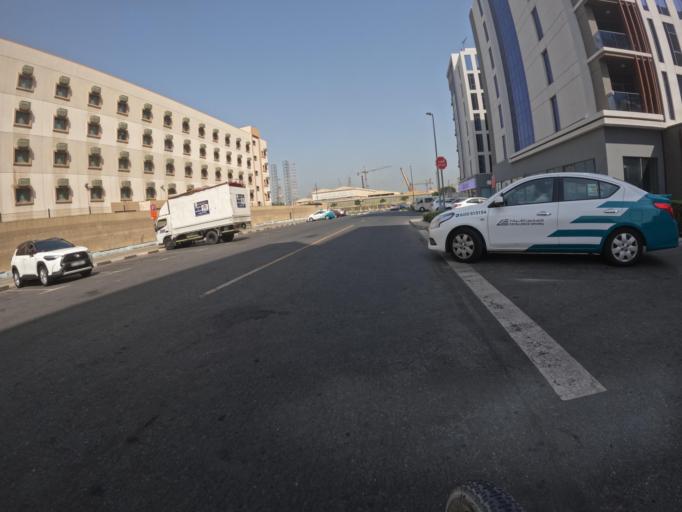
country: AE
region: Ash Shariqah
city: Sharjah
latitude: 25.2460
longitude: 55.2749
